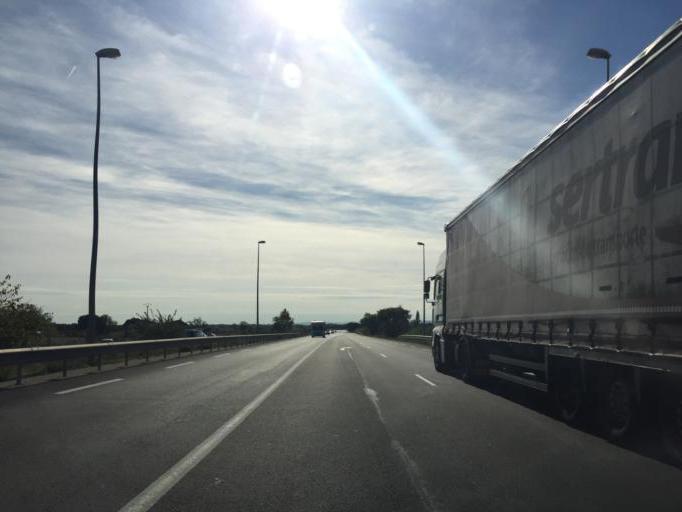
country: FR
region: Rhone-Alpes
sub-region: Departement de la Drome
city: Donzere
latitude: 44.4372
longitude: 4.7174
